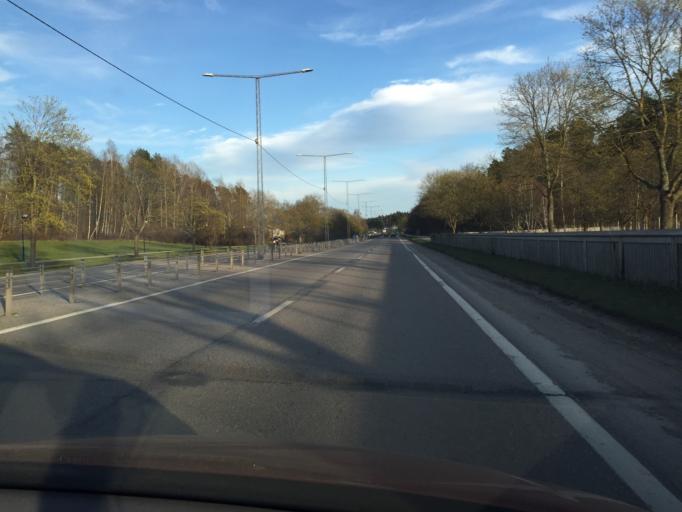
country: SE
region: Stockholm
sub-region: Stockholms Kommun
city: Bromma
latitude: 59.3509
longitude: 17.8864
